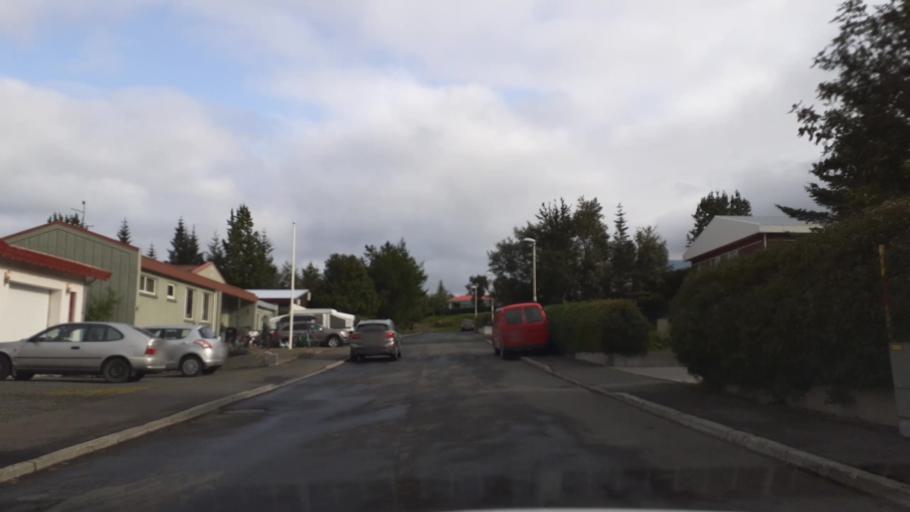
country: IS
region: Northeast
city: Akureyri
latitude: 65.7464
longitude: -18.0838
